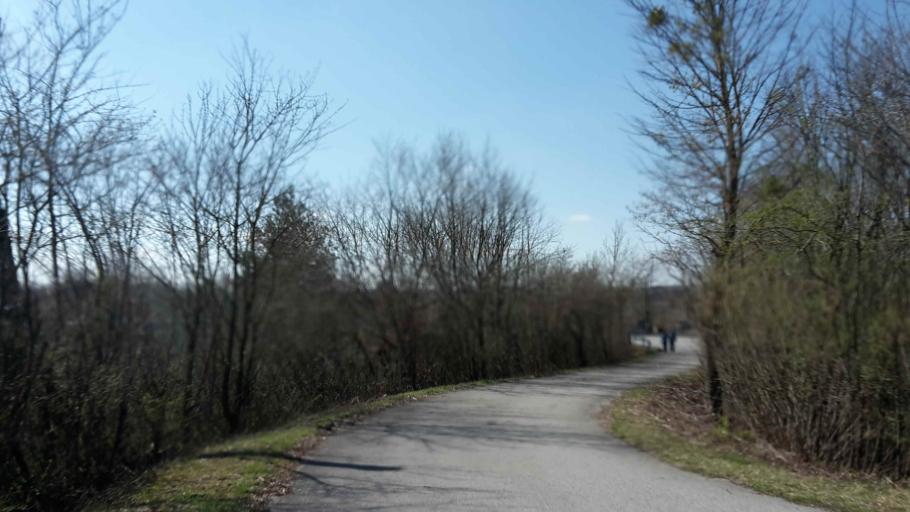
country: DE
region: Bavaria
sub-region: Upper Bavaria
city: Karlsfeld
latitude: 48.1982
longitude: 11.4858
